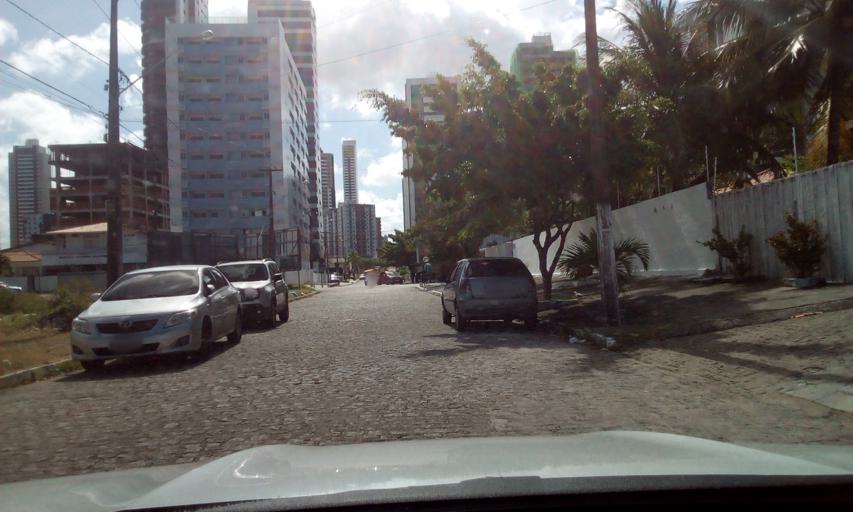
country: BR
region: Paraiba
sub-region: Joao Pessoa
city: Joao Pessoa
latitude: -7.1209
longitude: -34.8270
